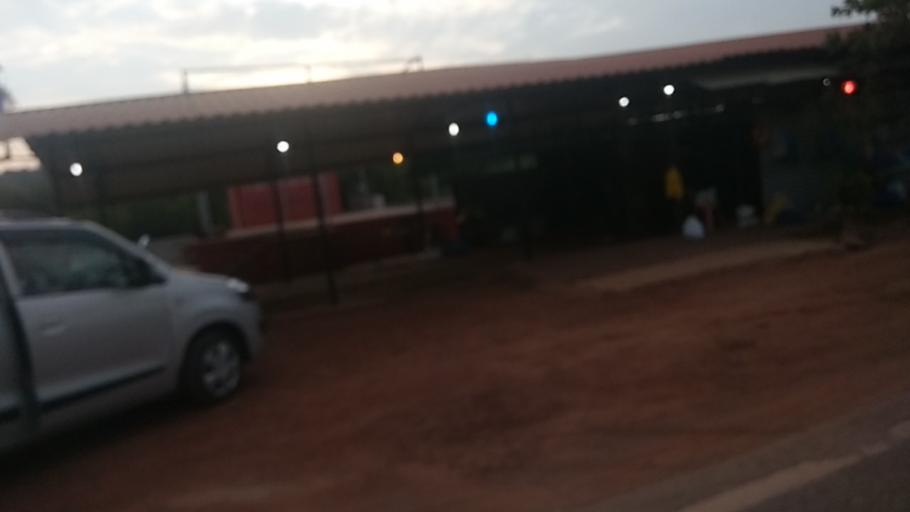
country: IN
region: Goa
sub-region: South Goa
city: Cortalim
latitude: 15.3954
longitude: 73.9127
